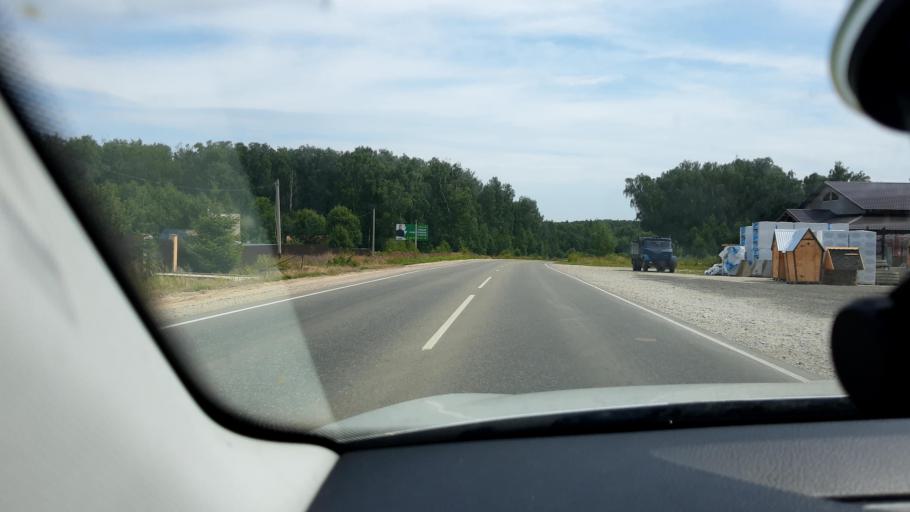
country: RU
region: Tula
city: Zaokskiy
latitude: 54.7455
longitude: 37.4118
